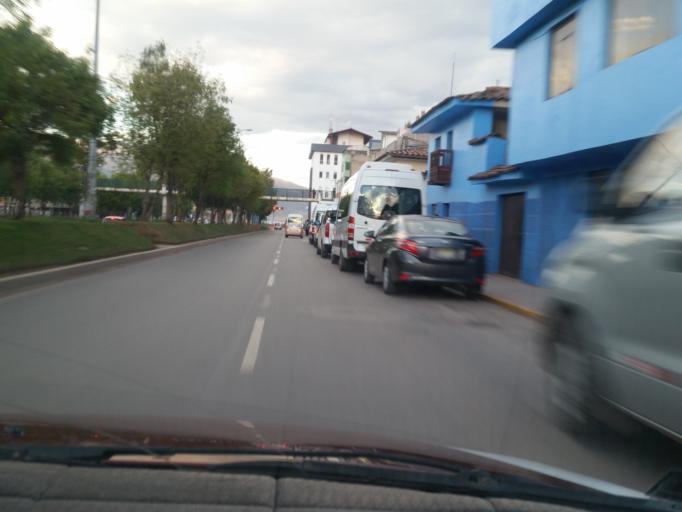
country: PE
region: Cusco
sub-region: Provincia de Cusco
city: Cusco
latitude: -13.5330
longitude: -71.9576
